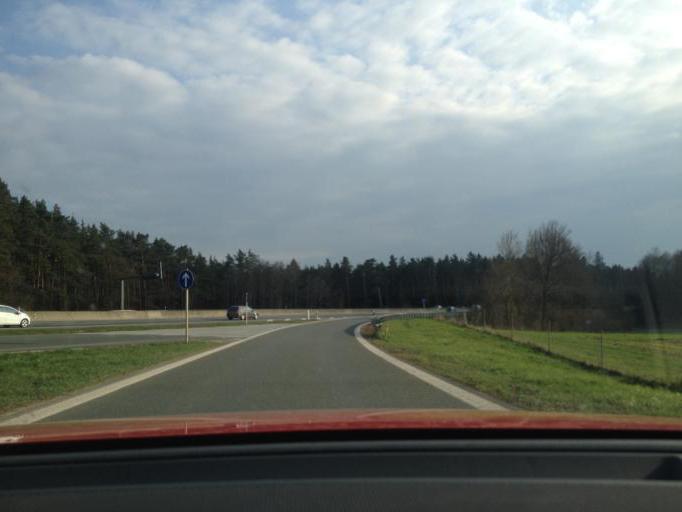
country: DE
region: Bavaria
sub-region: Upper Franconia
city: Pegnitz
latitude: 49.7307
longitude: 11.5111
